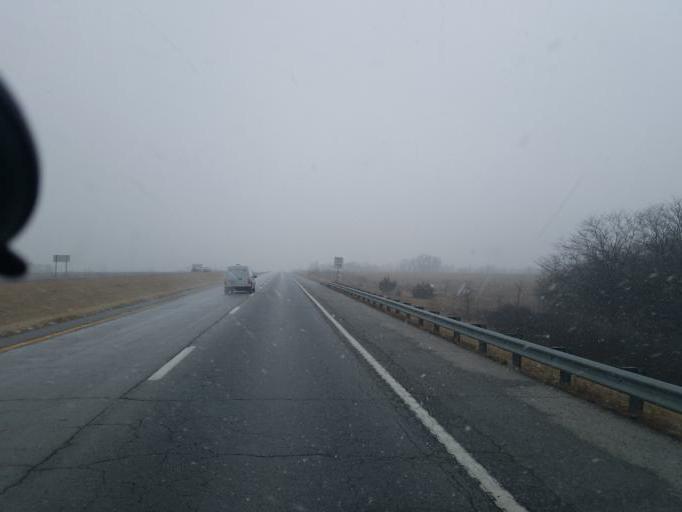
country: US
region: Missouri
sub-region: Macon County
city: La Plata
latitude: 39.9831
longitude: -92.4761
